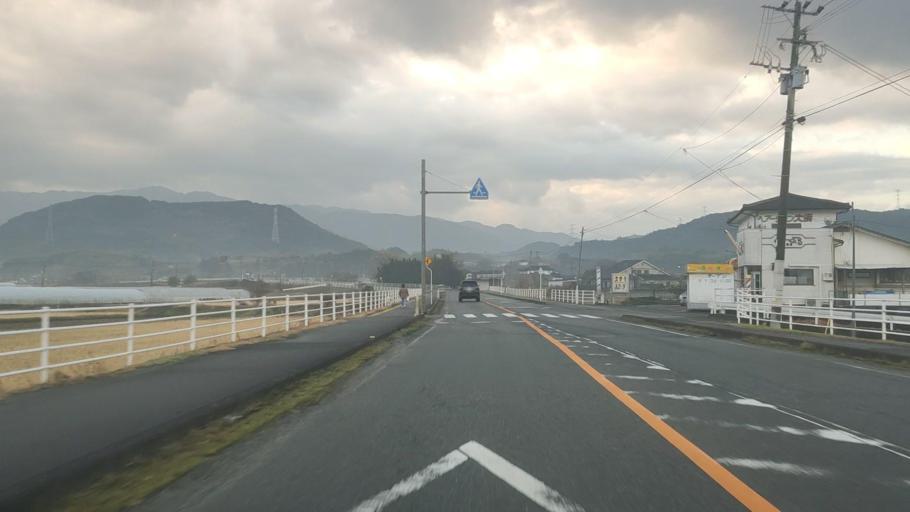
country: JP
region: Kumamoto
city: Matsubase
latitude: 32.6467
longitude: 130.8116
